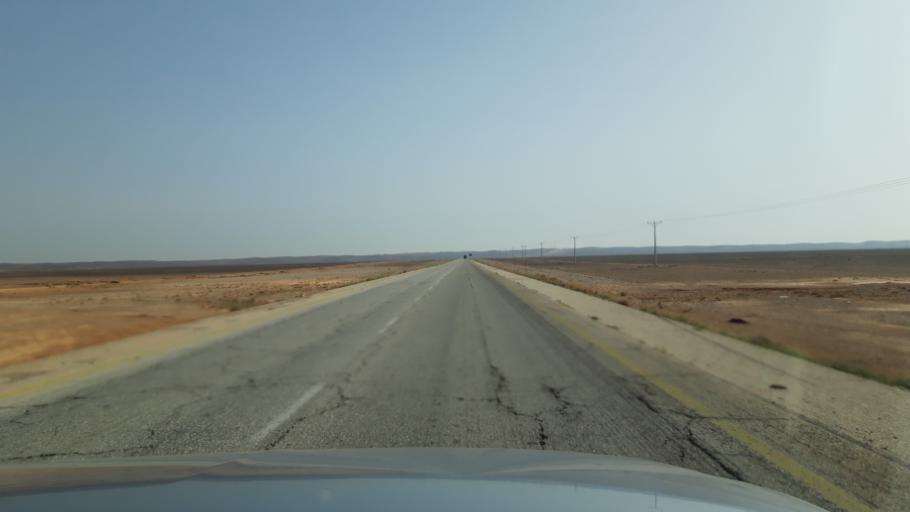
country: JO
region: Amman
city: Al Azraq ash Shamali
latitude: 31.8342
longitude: 36.6306
